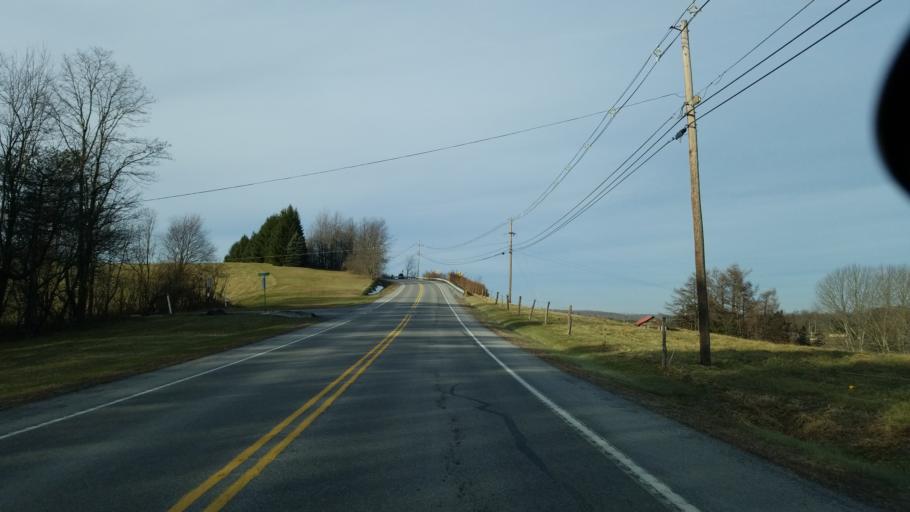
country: US
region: Pennsylvania
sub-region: Clearfield County
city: Curwensville
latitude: 40.9883
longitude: -78.6260
